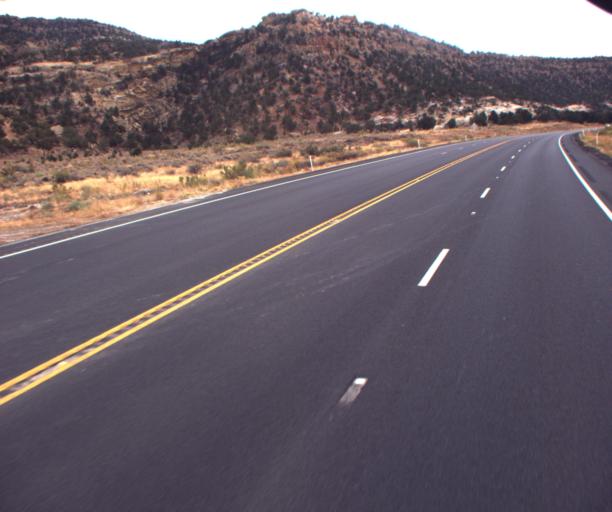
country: US
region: Arizona
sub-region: Navajo County
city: Kayenta
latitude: 36.5814
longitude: -110.4721
